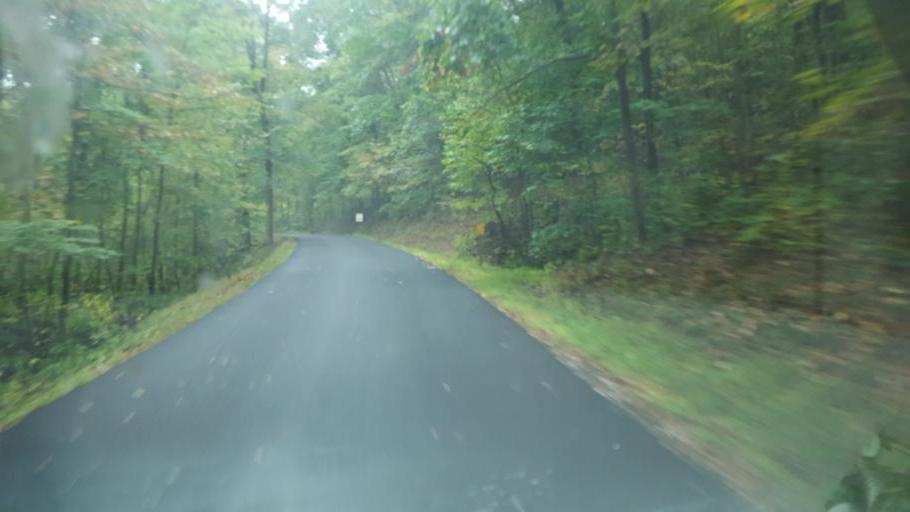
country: US
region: Ohio
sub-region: Ashland County
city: Loudonville
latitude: 40.6048
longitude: -82.3198
